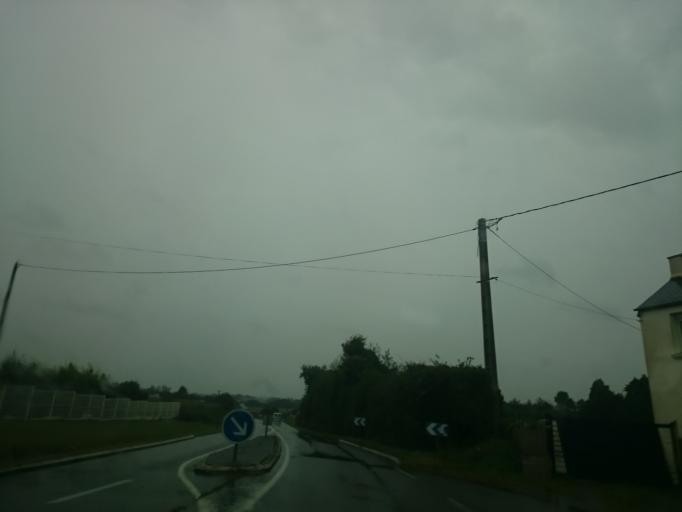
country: FR
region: Brittany
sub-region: Departement du Finistere
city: Plabennec
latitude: 48.5164
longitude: -4.4057
